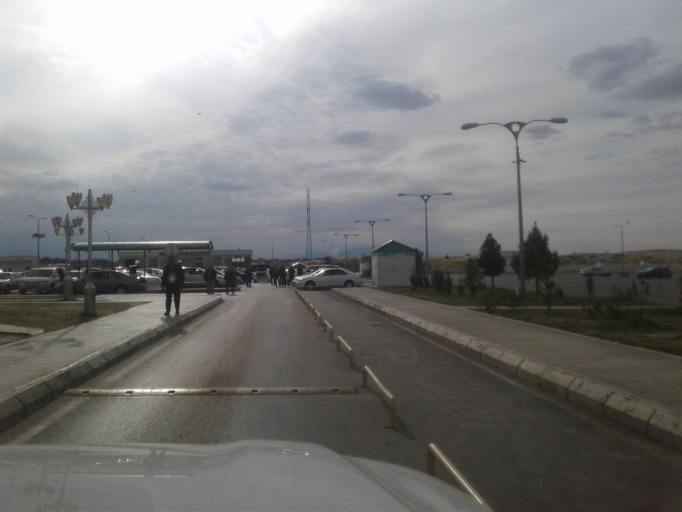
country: TM
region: Ahal
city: Ashgabat
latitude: 38.0501
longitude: 58.3983
